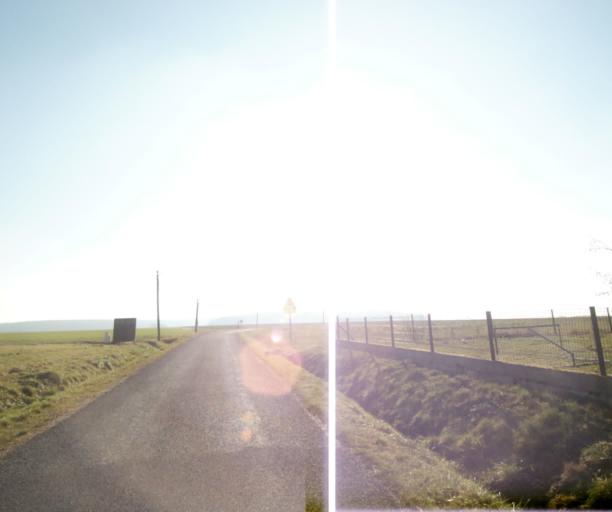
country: FR
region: Champagne-Ardenne
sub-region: Departement de la Haute-Marne
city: Bienville
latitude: 48.5397
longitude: 5.0187
